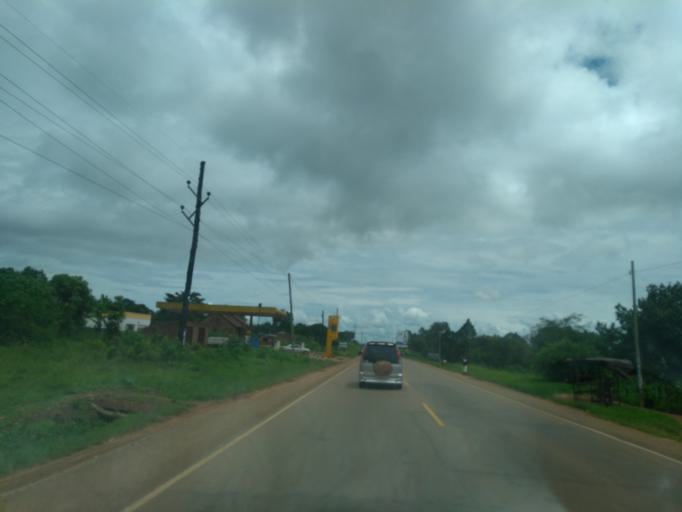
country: UG
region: Central Region
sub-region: Butambala District
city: Gombe
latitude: -0.0013
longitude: 32.0390
